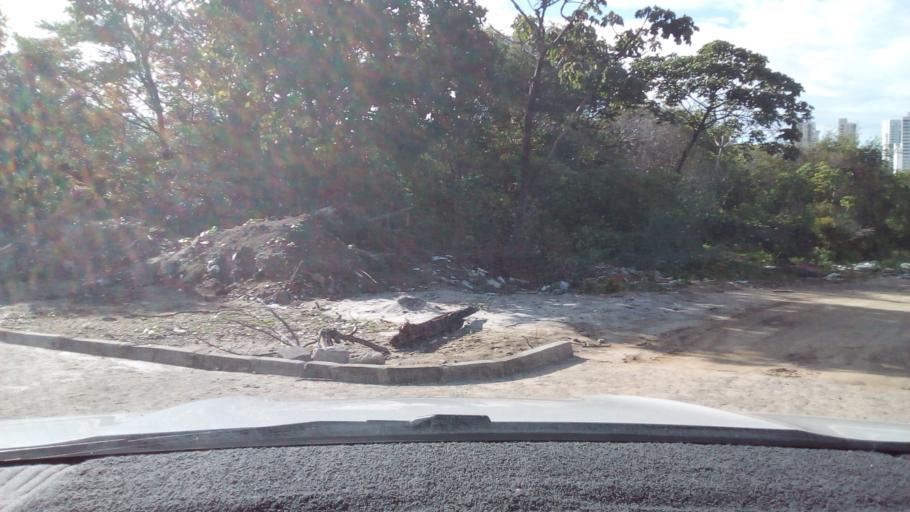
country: BR
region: Paraiba
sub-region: Joao Pessoa
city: Joao Pessoa
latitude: -7.1410
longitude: -34.8254
